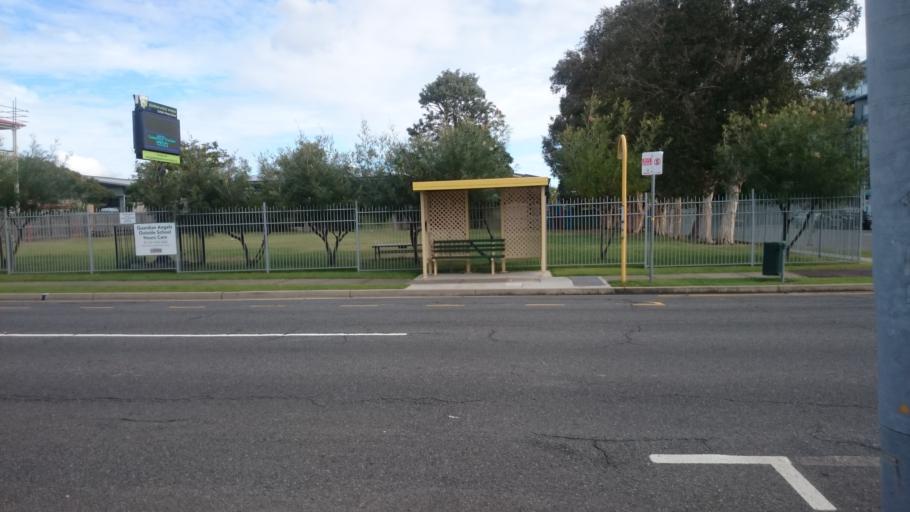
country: AU
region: Queensland
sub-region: Brisbane
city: Wynnum
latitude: -27.4458
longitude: 153.1757
